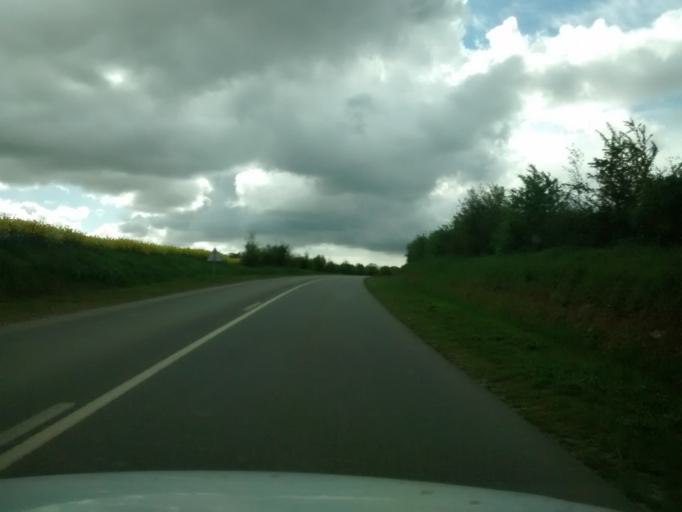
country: FR
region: Brittany
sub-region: Departement du Morbihan
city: Ruffiac
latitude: 47.8128
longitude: -2.2588
